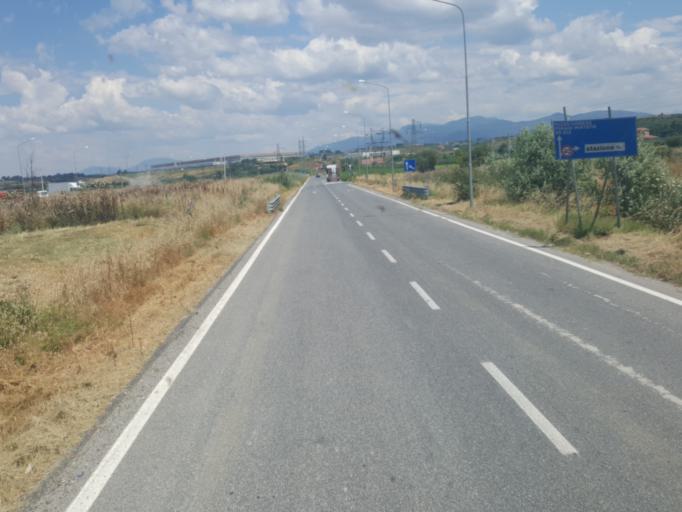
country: IT
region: Latium
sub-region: Citta metropolitana di Roma Capitale
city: Fiano Romano
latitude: 42.1557
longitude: 12.6427
